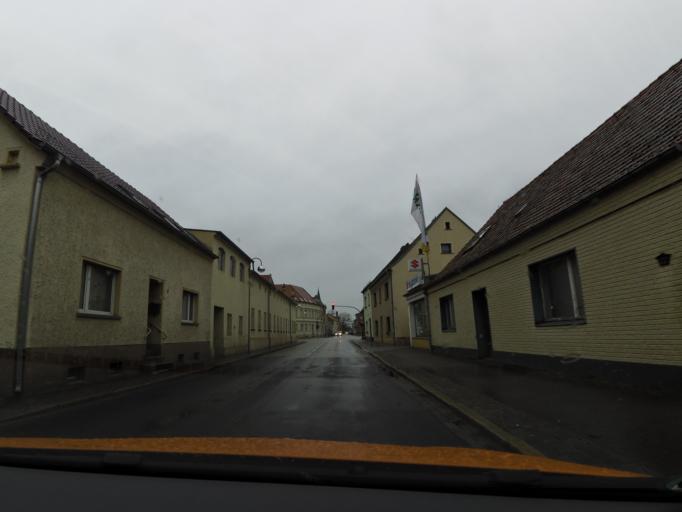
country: DE
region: Brandenburg
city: Zossen
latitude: 52.2137
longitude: 13.4457
